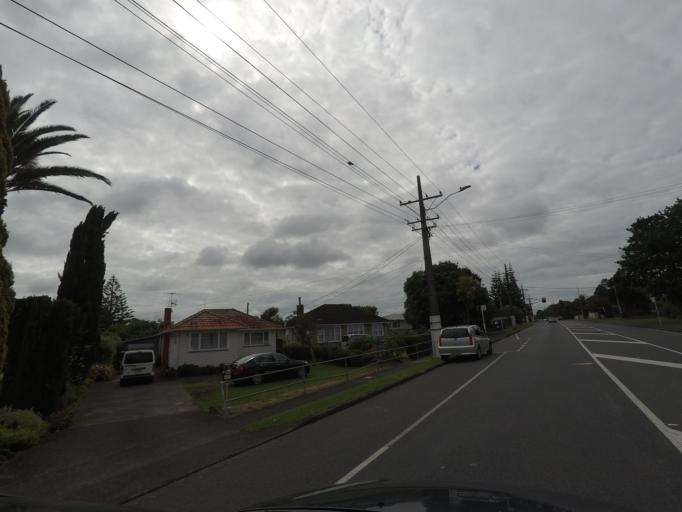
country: NZ
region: Auckland
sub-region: Auckland
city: Rosebank
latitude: -36.8702
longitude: 174.6192
